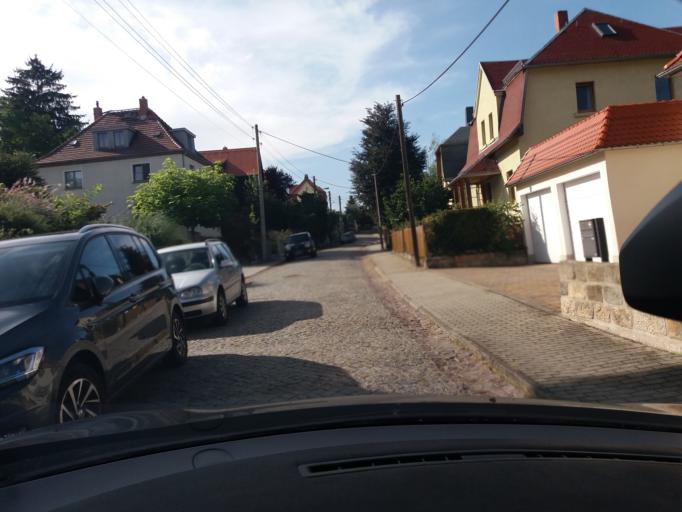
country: DE
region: Saxony
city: Radebeul
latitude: 51.0786
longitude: 13.6492
